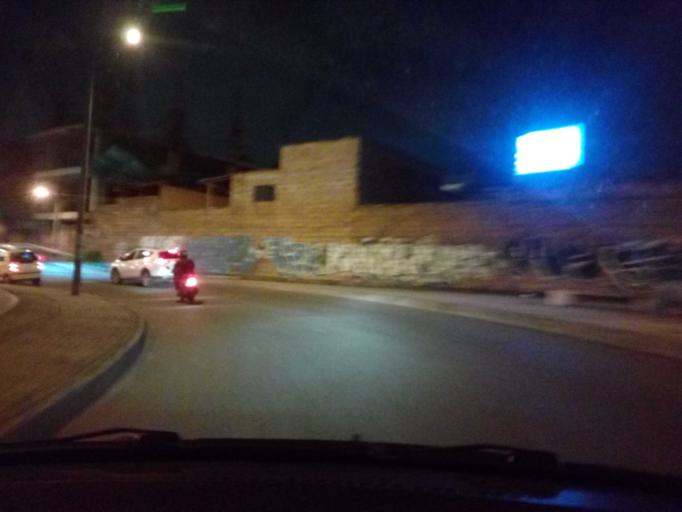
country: CO
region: Antioquia
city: Itagui
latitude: 6.1923
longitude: -75.5932
